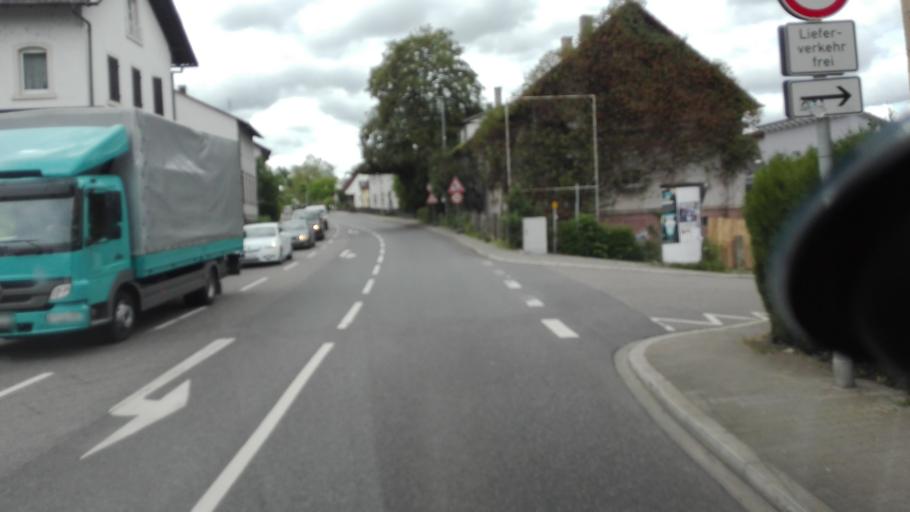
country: DE
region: Baden-Wuerttemberg
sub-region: Karlsruhe Region
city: Kronau
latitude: 49.2189
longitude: 8.6528
